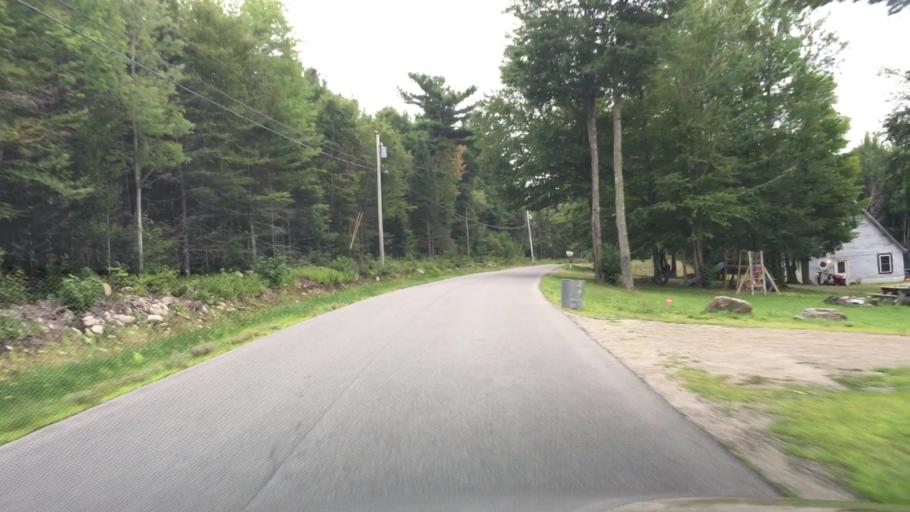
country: US
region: Maine
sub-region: Waldo County
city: Stockton Springs
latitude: 44.5151
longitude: -68.8755
